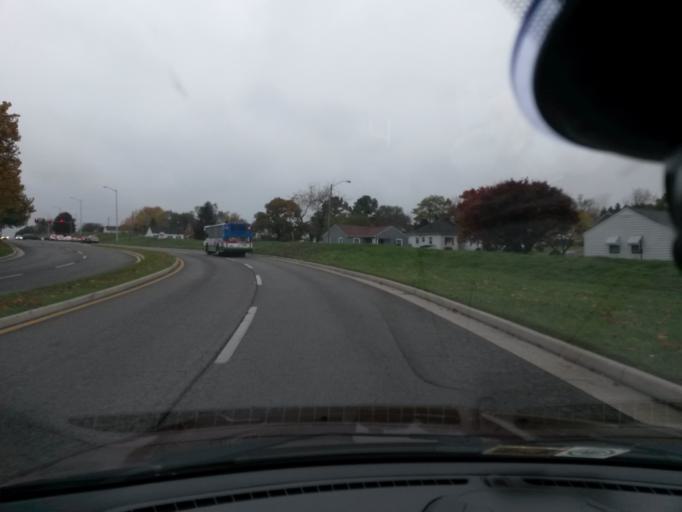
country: US
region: Virginia
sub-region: Roanoke County
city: Hollins
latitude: 37.3071
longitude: -79.9610
